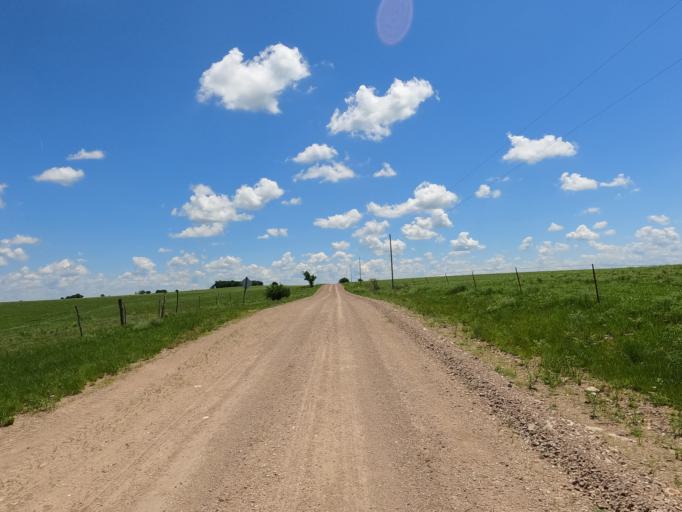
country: US
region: Kansas
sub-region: Chase County
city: Cottonwood Falls
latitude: 38.2167
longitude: -96.7666
